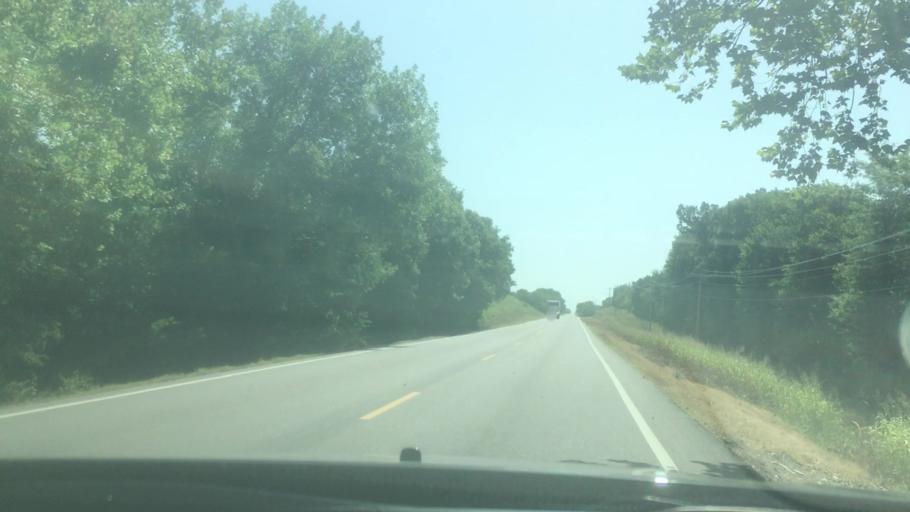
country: US
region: Oklahoma
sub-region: Bryan County
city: Durant
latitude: 34.1427
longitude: -96.3960
